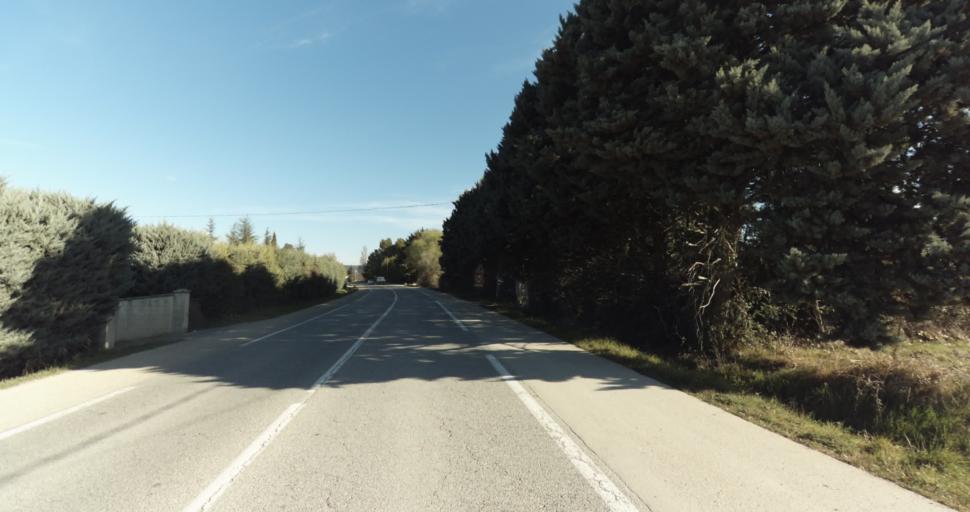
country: FR
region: Provence-Alpes-Cote d'Azur
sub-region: Departement des Bouches-du-Rhone
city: Aix-en-Provence
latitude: 43.5646
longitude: 5.4342
